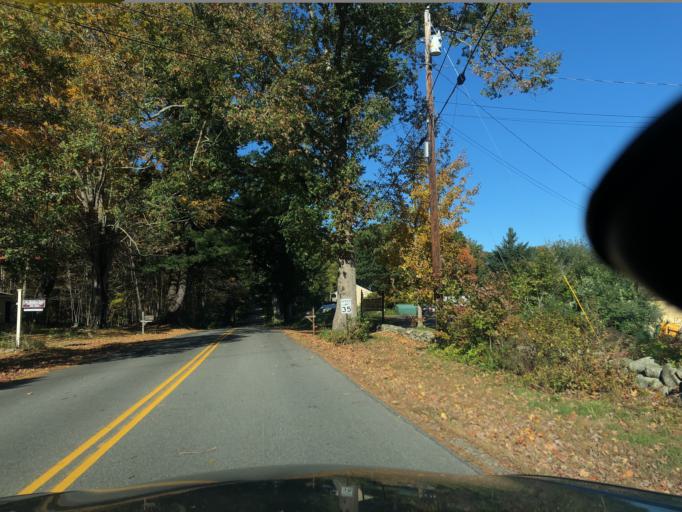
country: US
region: New Hampshire
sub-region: Strafford County
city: Lee
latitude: 43.1166
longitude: -70.9722
